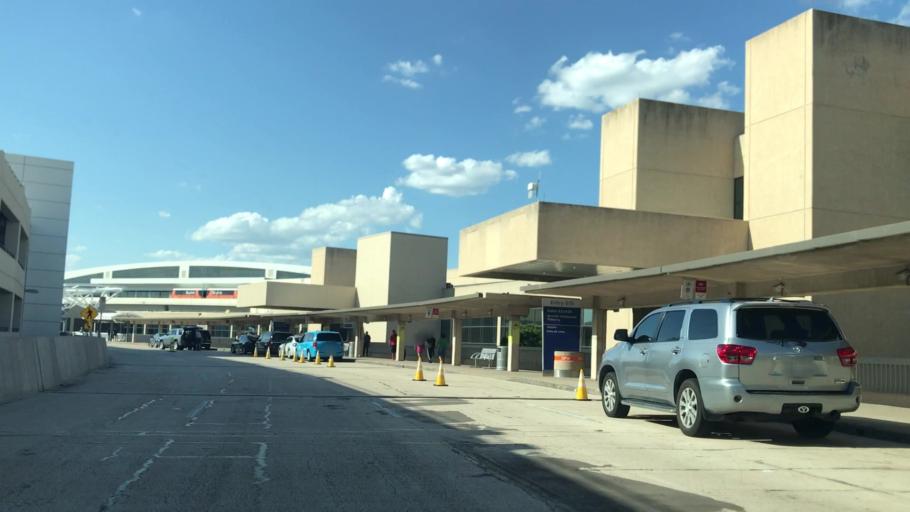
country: US
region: Texas
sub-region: Tarrant County
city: Grapevine
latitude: 32.8902
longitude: -97.0363
